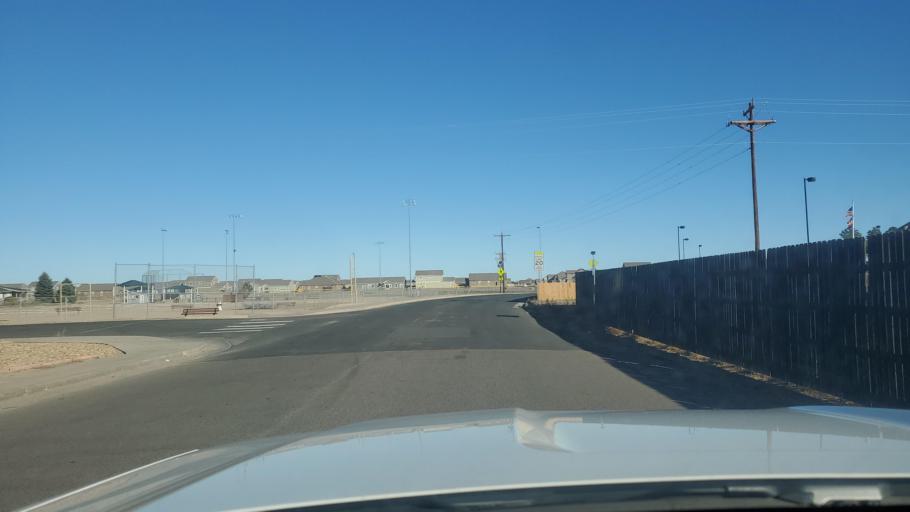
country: US
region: Colorado
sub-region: Adams County
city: Strasburg
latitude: 39.7451
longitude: -104.3265
